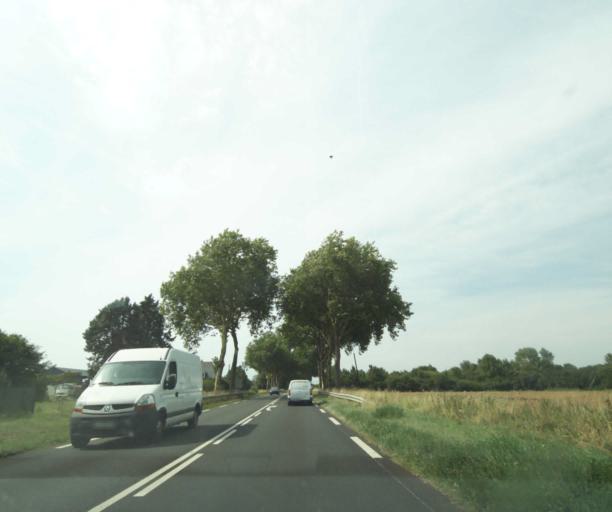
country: FR
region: Centre
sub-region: Departement d'Indre-et-Loire
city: Charentilly
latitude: 47.4574
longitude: 0.6257
